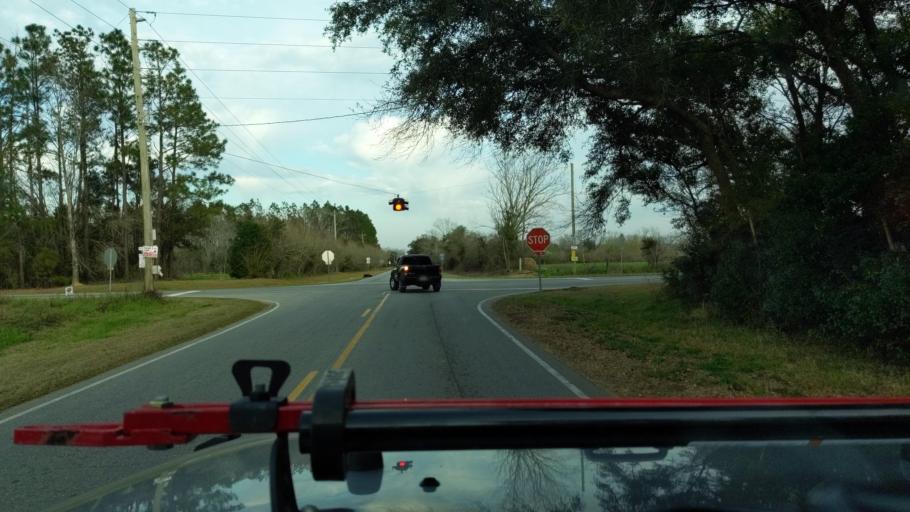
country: US
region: Alabama
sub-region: Baldwin County
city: Foley
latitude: 30.4579
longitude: -87.7428
